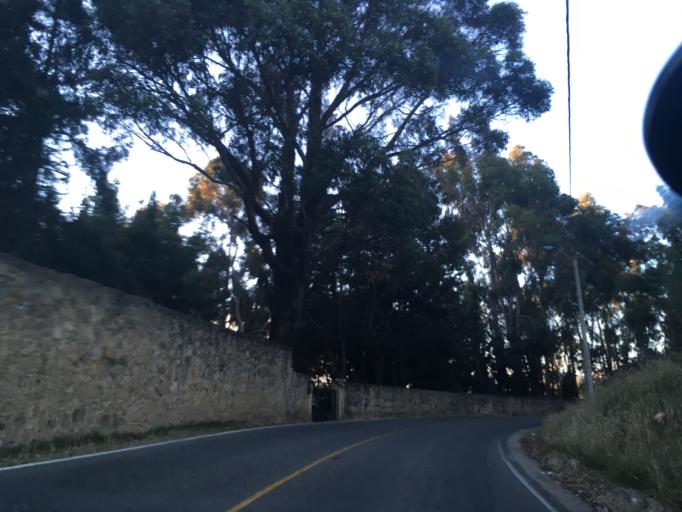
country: CO
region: Boyaca
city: Aquitania
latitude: 5.5435
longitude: -72.8843
